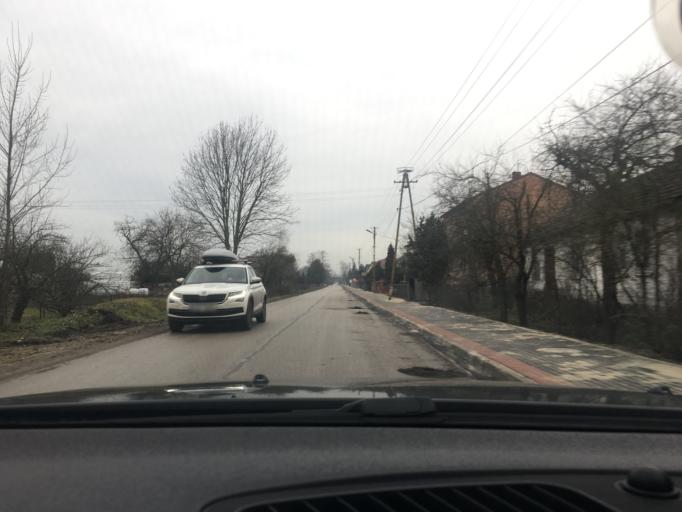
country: PL
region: Swietokrzyskie
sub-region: Powiat jedrzejowski
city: Imielno
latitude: 50.6421
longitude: 20.3879
